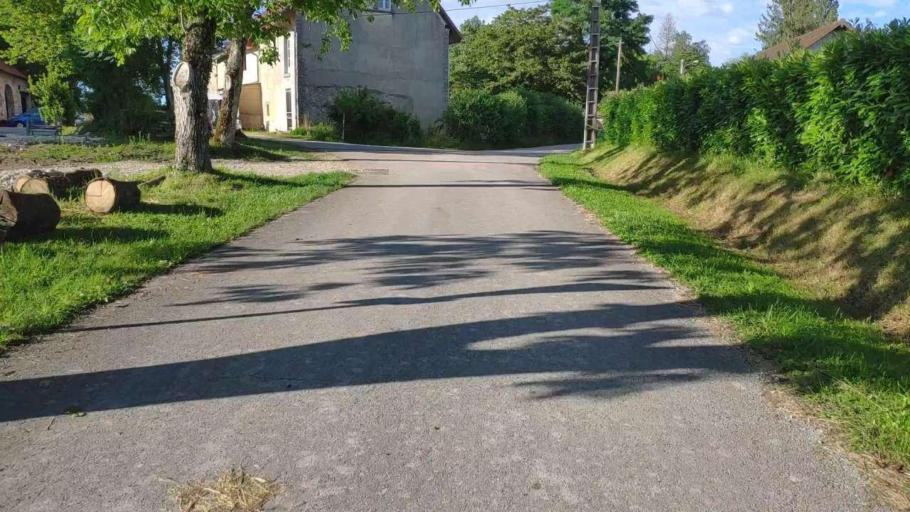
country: FR
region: Franche-Comte
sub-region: Departement du Jura
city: Bletterans
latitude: 46.7820
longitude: 5.4891
